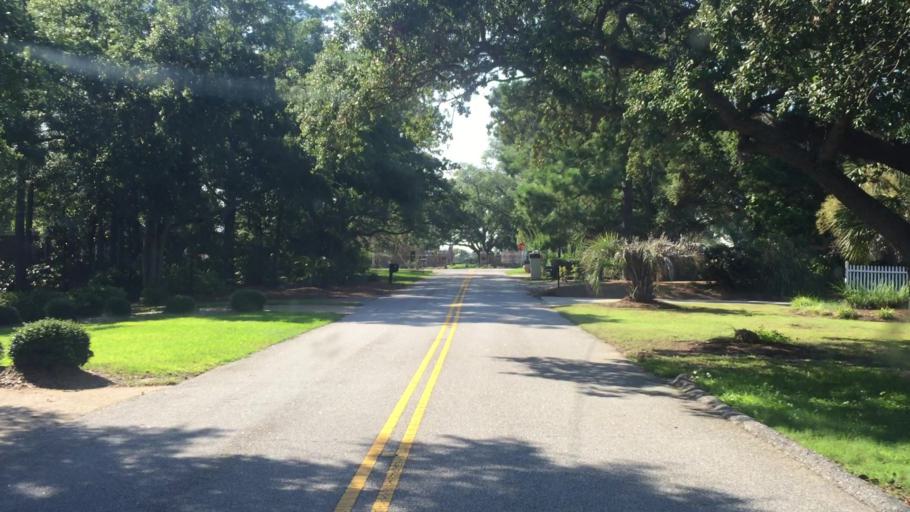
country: US
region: South Carolina
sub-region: Horry County
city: Myrtle Beach
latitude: 33.7454
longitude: -78.8135
